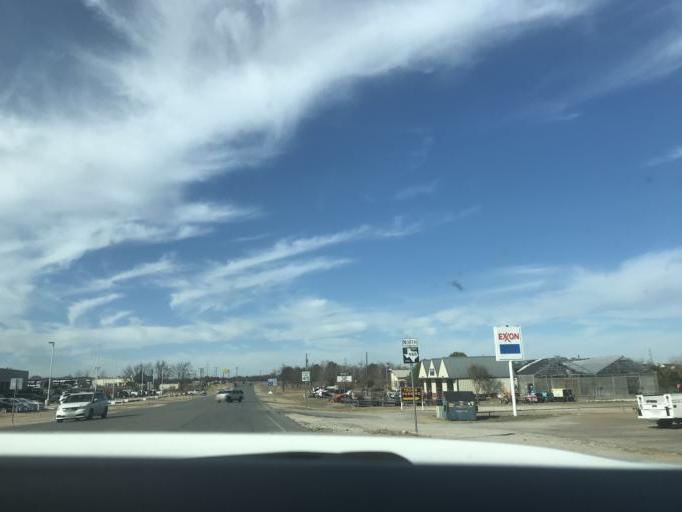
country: US
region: Texas
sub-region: Erath County
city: Stephenville
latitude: 32.2021
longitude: -98.2462
